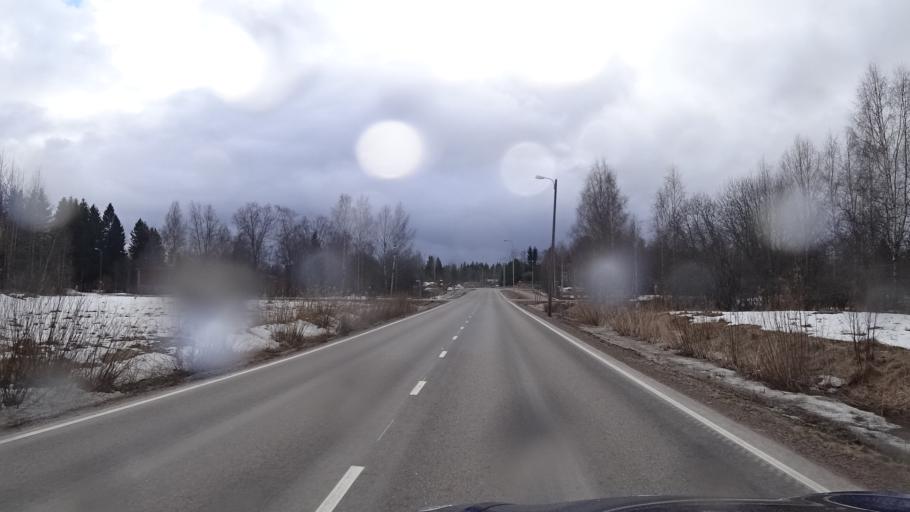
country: FI
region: Kymenlaakso
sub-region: Kotka-Hamina
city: Karhula
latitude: 60.5408
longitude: 26.9074
